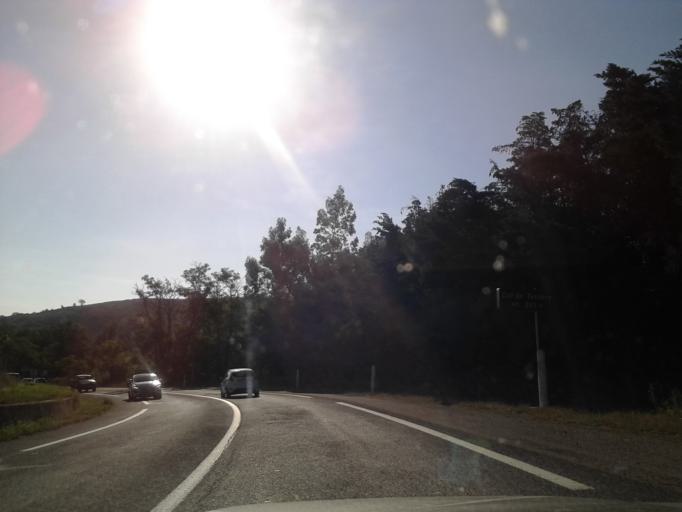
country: FR
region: Languedoc-Roussillon
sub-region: Departement des Pyrenees-Orientales
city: Vinca
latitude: 42.6453
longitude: 2.5610
